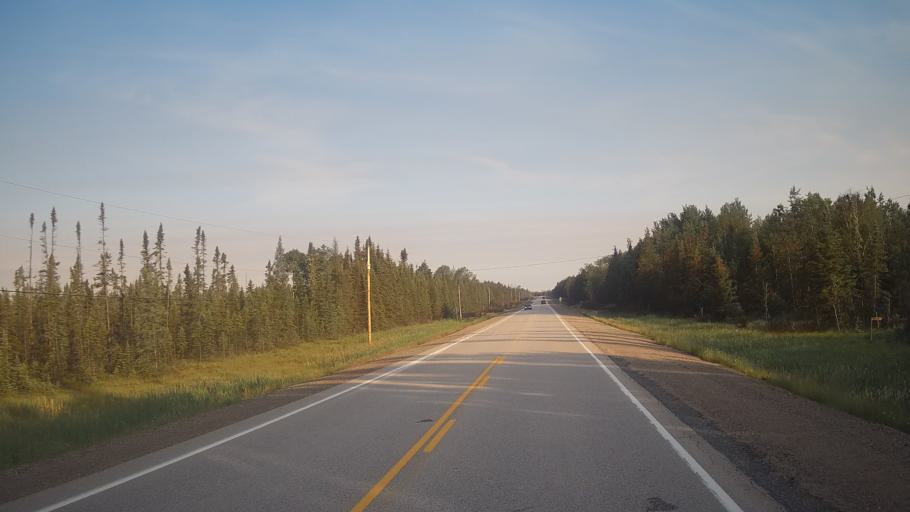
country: CA
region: Ontario
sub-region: Rainy River District
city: Atikokan
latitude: 49.2561
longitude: -91.1259
